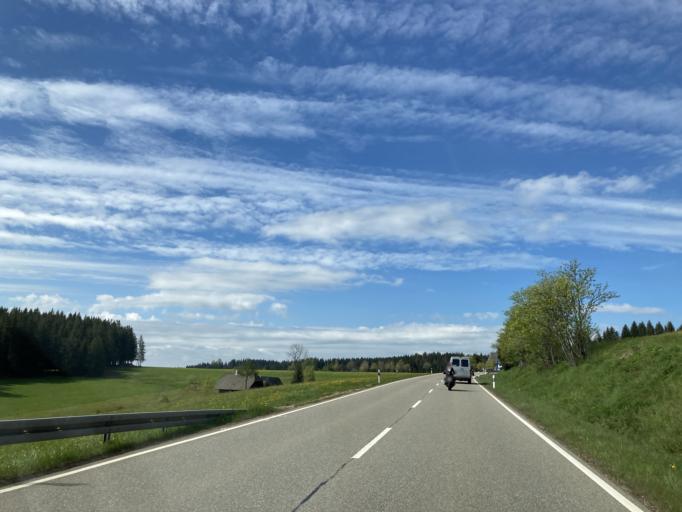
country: DE
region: Baden-Wuerttemberg
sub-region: Freiburg Region
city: Schonwald im Schwarzwald
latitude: 48.0916
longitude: 8.2015
